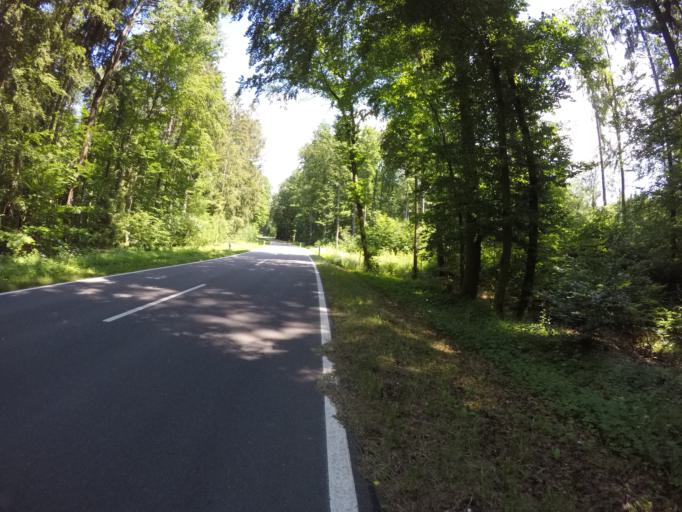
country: DE
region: Bavaria
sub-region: Lower Bavaria
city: Essing
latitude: 48.9089
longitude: 11.7828
